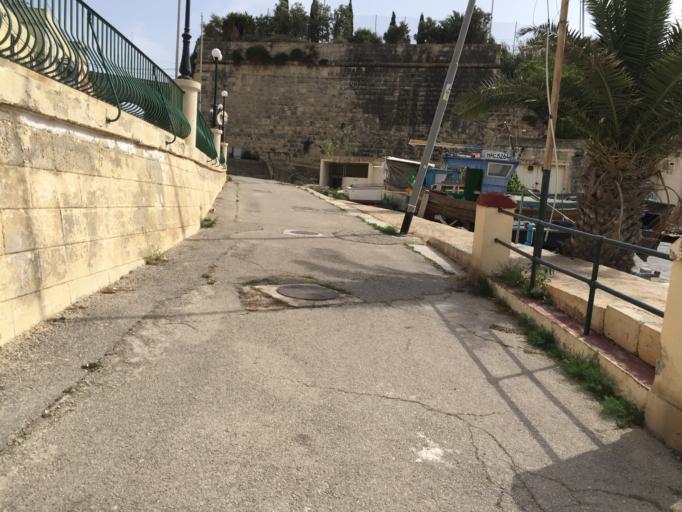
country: MT
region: Bormla
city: Cospicua
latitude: 35.8875
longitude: 14.5261
